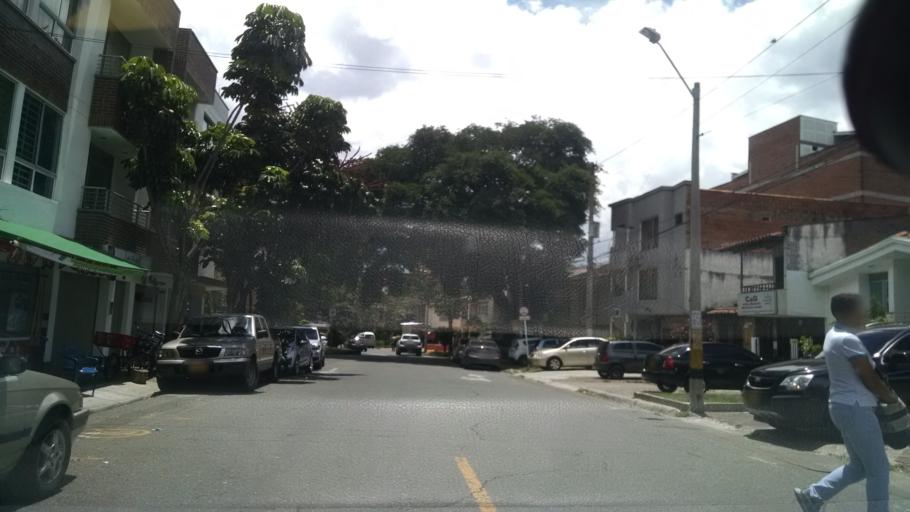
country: CO
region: Antioquia
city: Medellin
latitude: 6.2630
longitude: -75.5959
